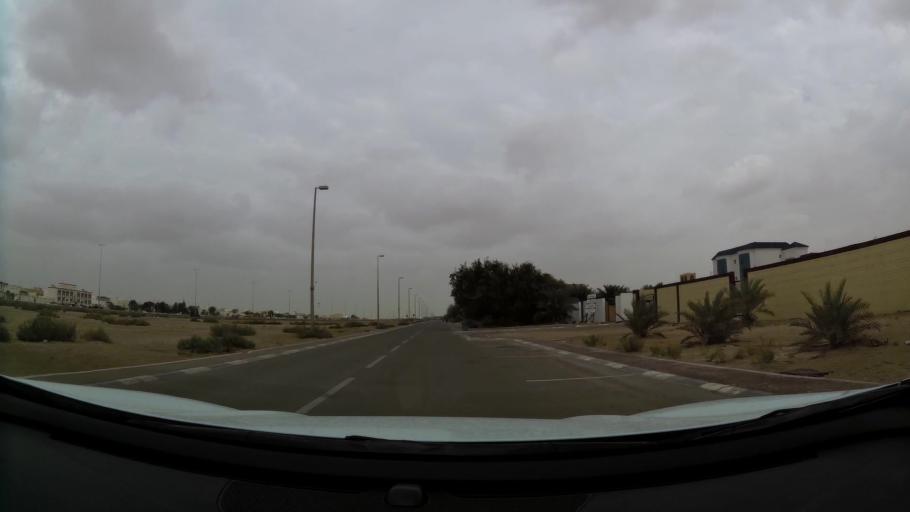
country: AE
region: Abu Dhabi
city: Abu Dhabi
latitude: 24.3510
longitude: 54.6536
